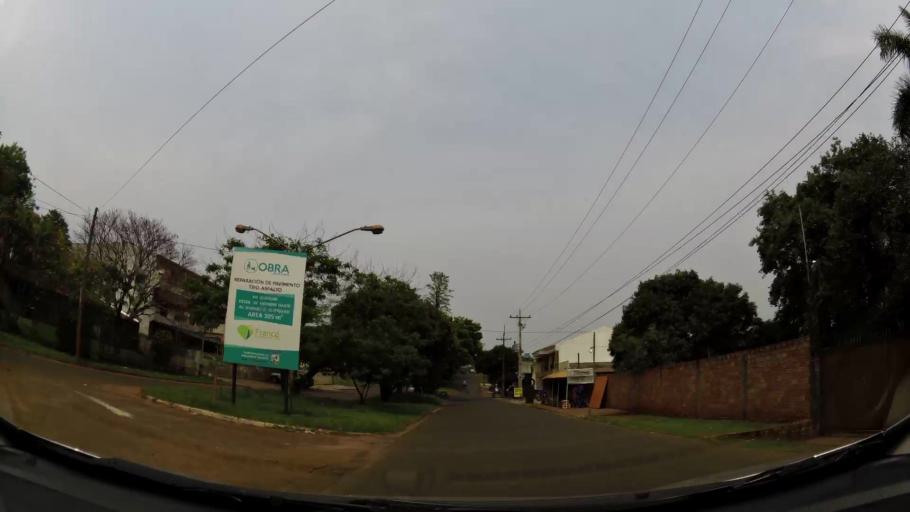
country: PY
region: Alto Parana
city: Presidente Franco
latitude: -25.5506
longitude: -54.6272
